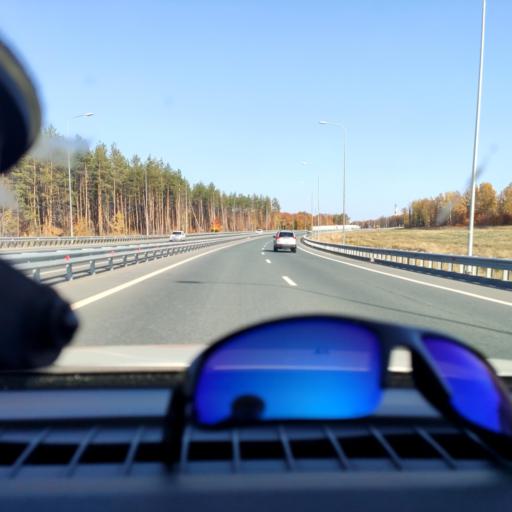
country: RU
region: Samara
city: Bereza
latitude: 53.5051
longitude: 50.1216
